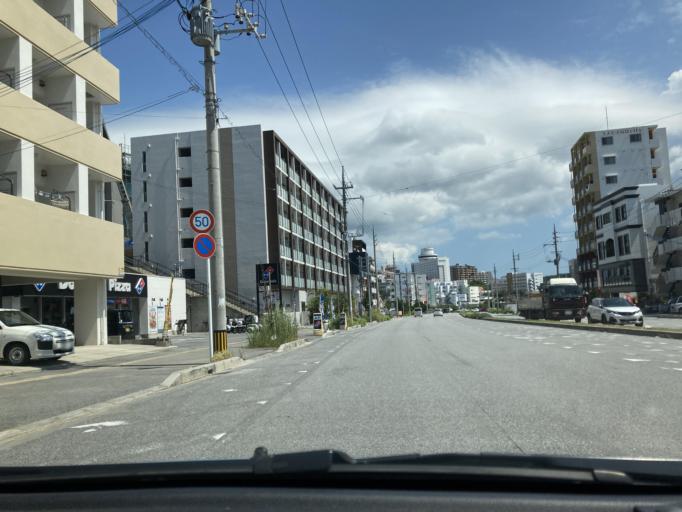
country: JP
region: Okinawa
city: Naha-shi
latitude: 26.2217
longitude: 127.7006
